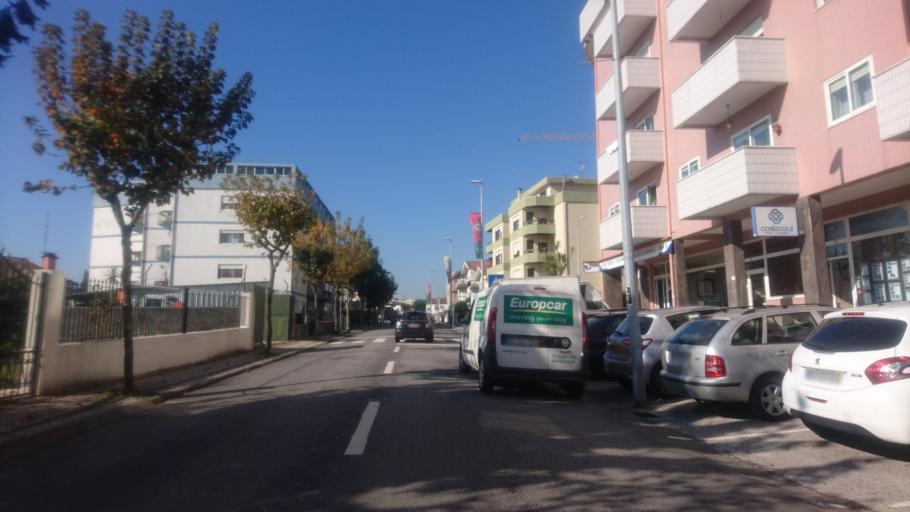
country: PT
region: Aveiro
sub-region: Santa Maria da Feira
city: Feira
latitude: 40.9262
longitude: -8.5534
